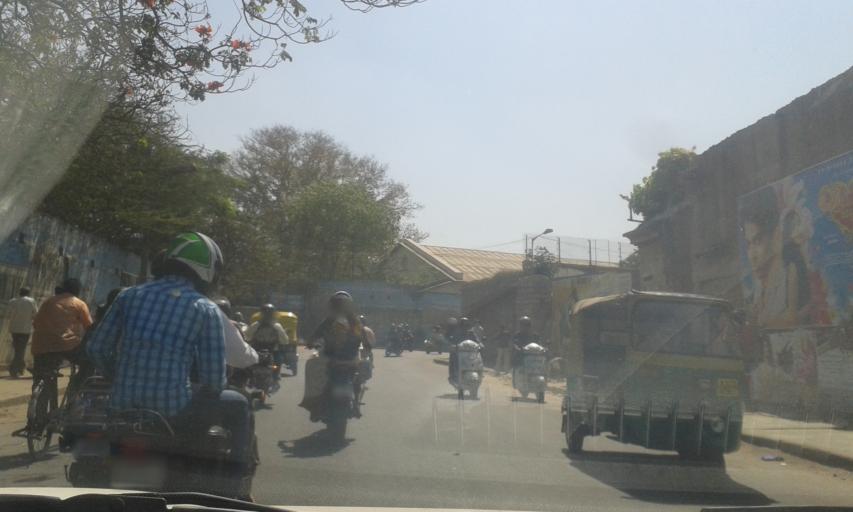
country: IN
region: Karnataka
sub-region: Bangalore Urban
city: Bangalore
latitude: 12.9704
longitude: 77.5668
